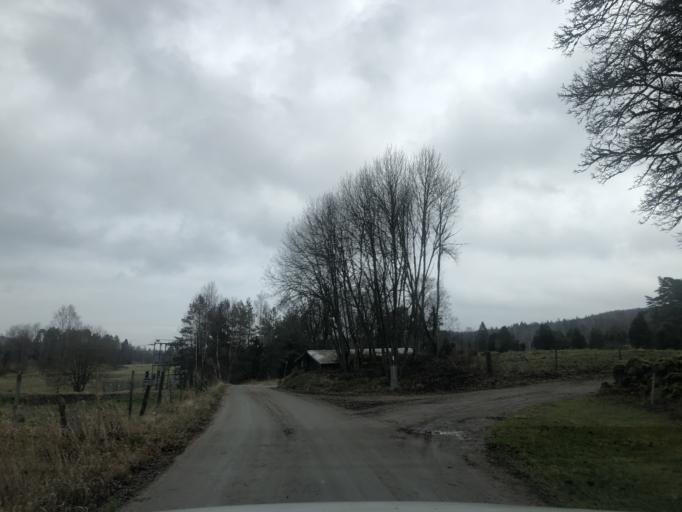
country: SE
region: Vaestra Goetaland
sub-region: Ulricehamns Kommun
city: Ulricehamn
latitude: 57.8861
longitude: 13.4629
